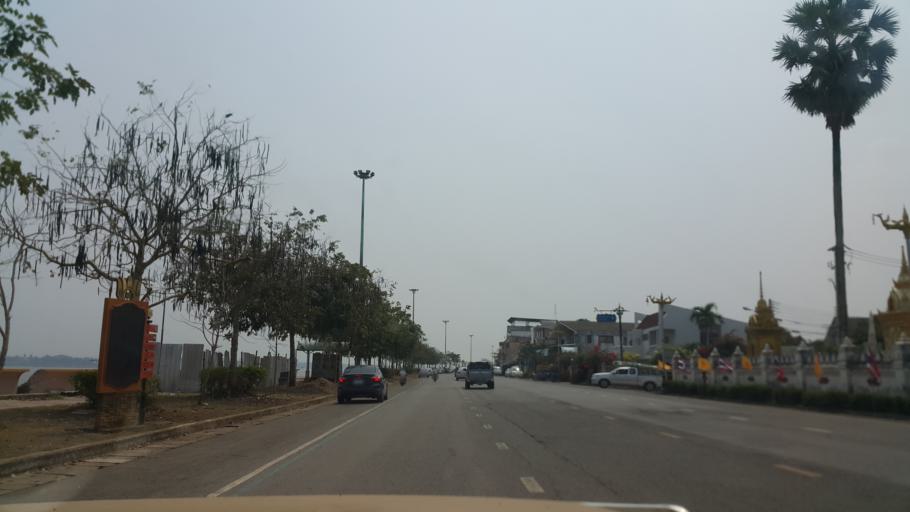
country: TH
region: Nakhon Phanom
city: Nakhon Phanom
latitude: 17.3978
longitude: 104.7910
